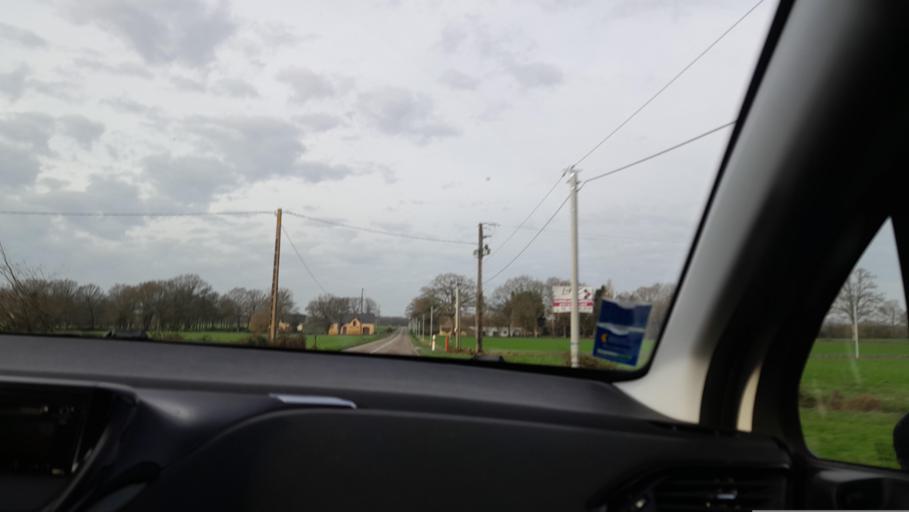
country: FR
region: Brittany
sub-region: Departement d'Ille-et-Vilaine
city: La Guerche-de-Bretagne
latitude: 47.9017
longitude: -1.1616
